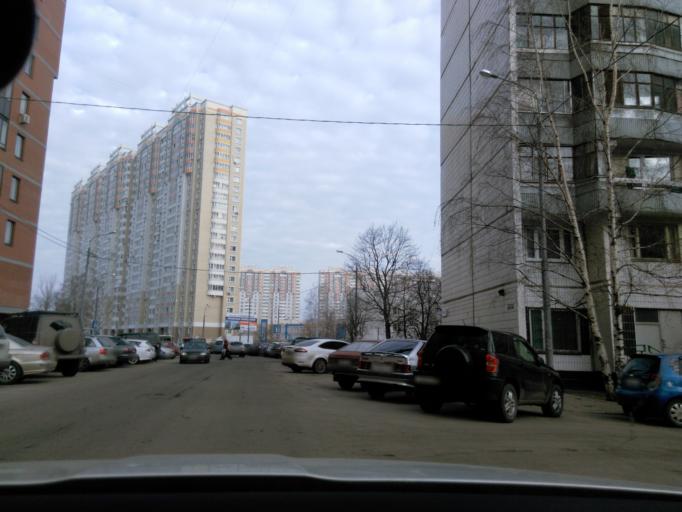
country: RU
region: Moskovskaya
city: Levoberezhnaya
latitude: 55.8974
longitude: 37.4802
